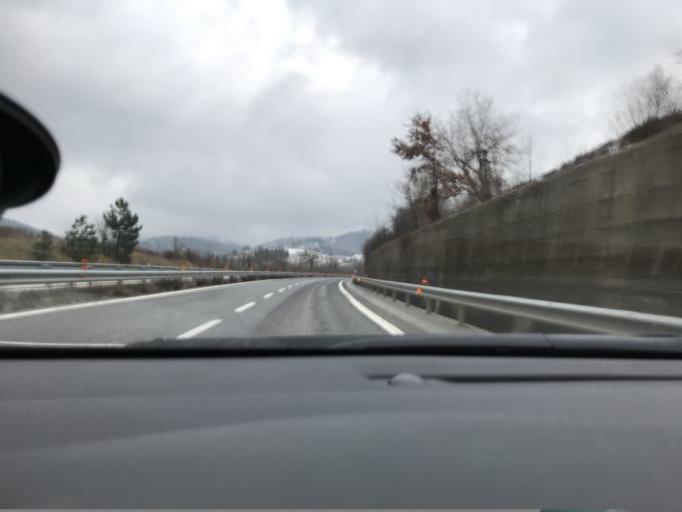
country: IT
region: The Marches
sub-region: Provincia di Ancona
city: Fabriano
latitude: 43.3284
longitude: 12.9235
